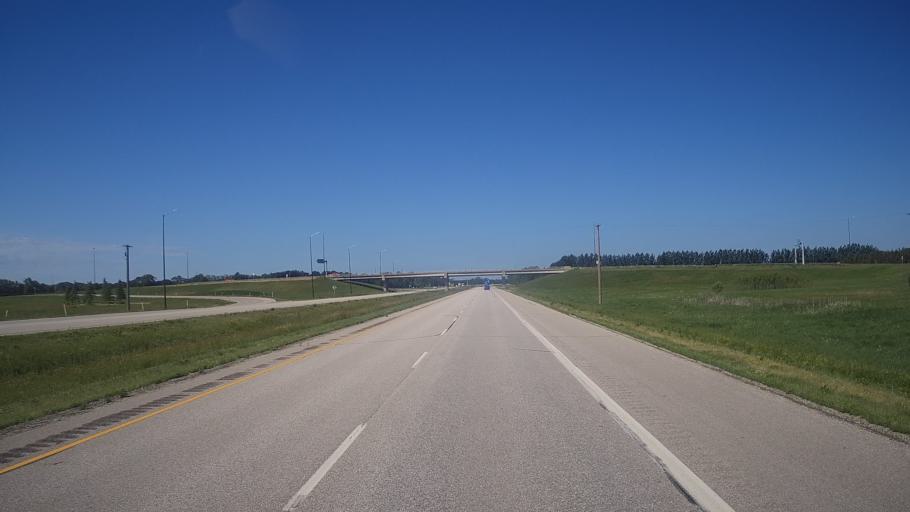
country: CA
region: Manitoba
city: Portage la Prairie
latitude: 49.9558
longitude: -98.2704
